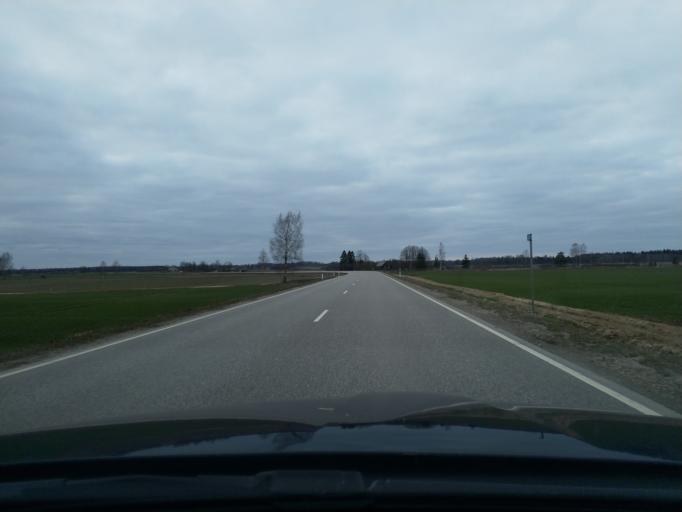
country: LV
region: Talsu Rajons
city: Sabile
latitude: 56.9339
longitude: 22.5166
